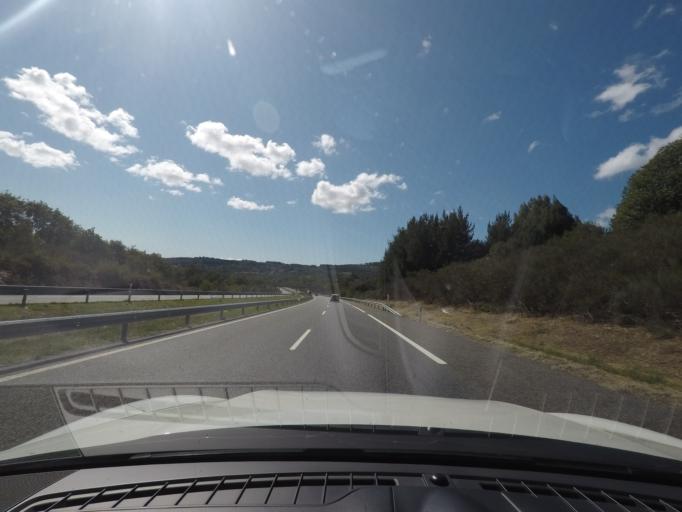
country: ES
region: Galicia
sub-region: Provincia de Ourense
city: Rios
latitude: 41.9798
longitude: -7.3099
